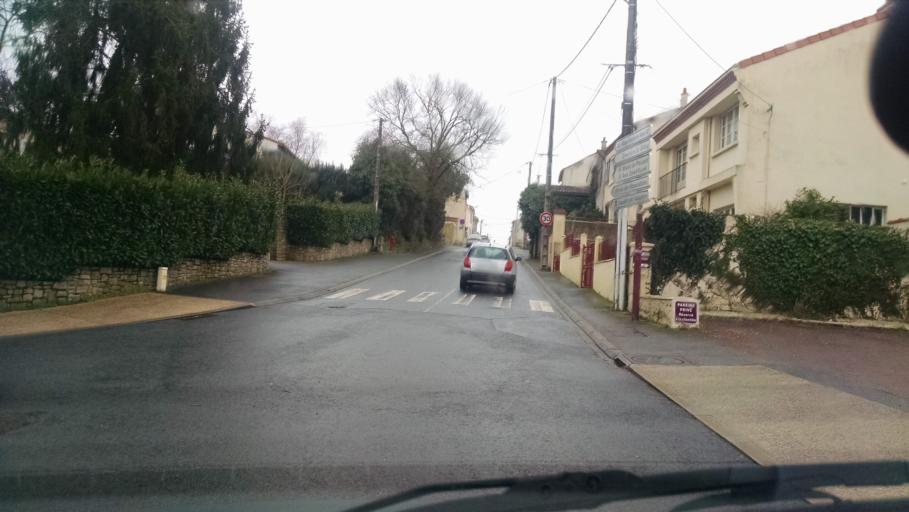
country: FR
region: Pays de la Loire
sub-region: Departement de la Loire-Atlantique
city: Clisson
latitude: 47.0849
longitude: -1.2804
